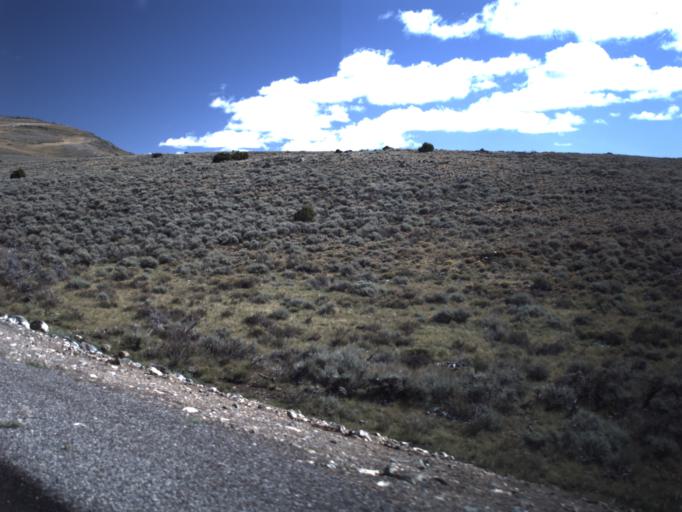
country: US
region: Utah
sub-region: Wayne County
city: Loa
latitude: 38.5022
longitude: -111.7985
